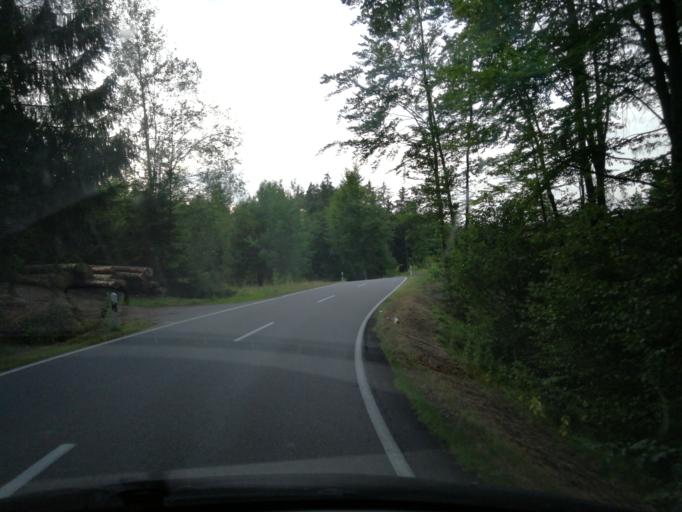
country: DE
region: Bavaria
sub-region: Lower Bavaria
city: Haibach
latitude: 49.0338
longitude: 12.7285
